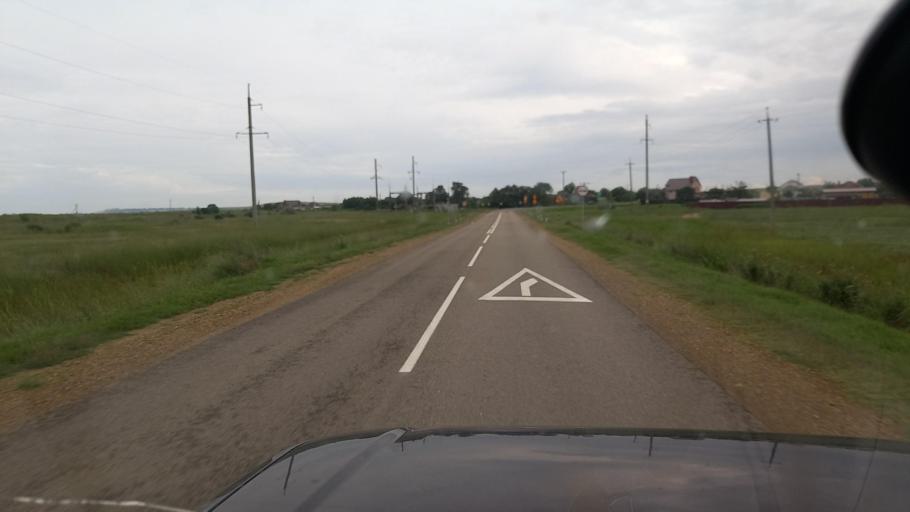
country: RU
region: Krasnodarskiy
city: Akhtanizovskaya
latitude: 45.3364
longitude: 37.1182
